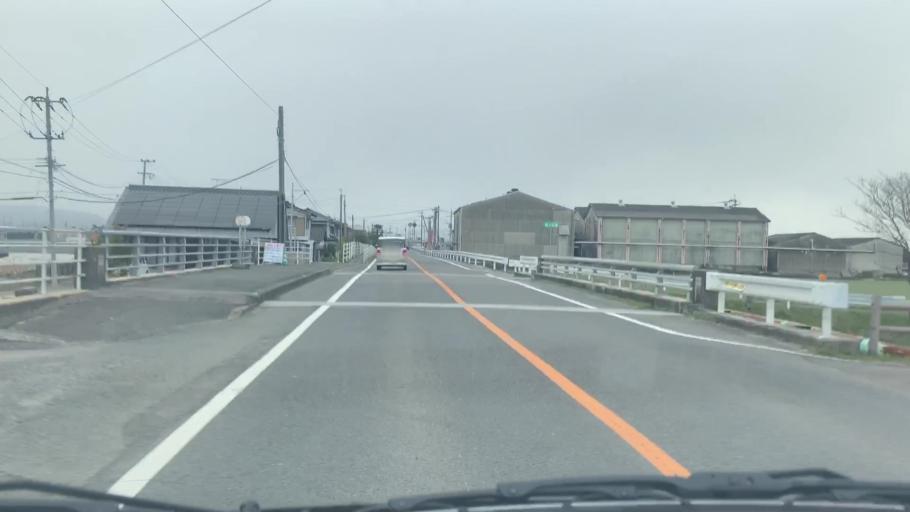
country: JP
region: Saga Prefecture
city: Saga-shi
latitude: 33.1907
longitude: 130.1928
